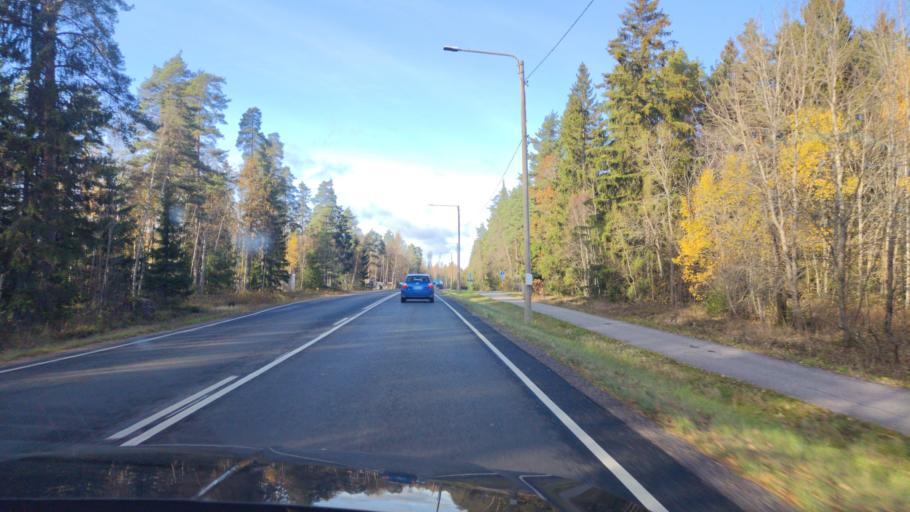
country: FI
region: Varsinais-Suomi
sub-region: Turku
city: Kaarina
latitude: 60.4542
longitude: 22.3691
